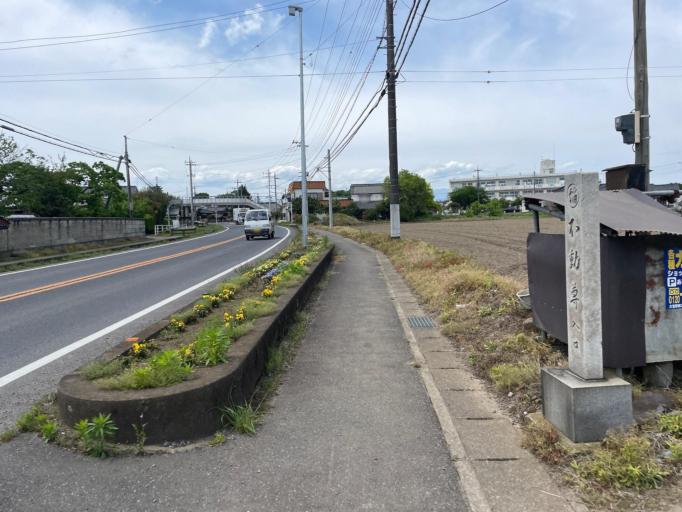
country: JP
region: Tochigi
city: Mibu
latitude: 36.4489
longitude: 139.7789
